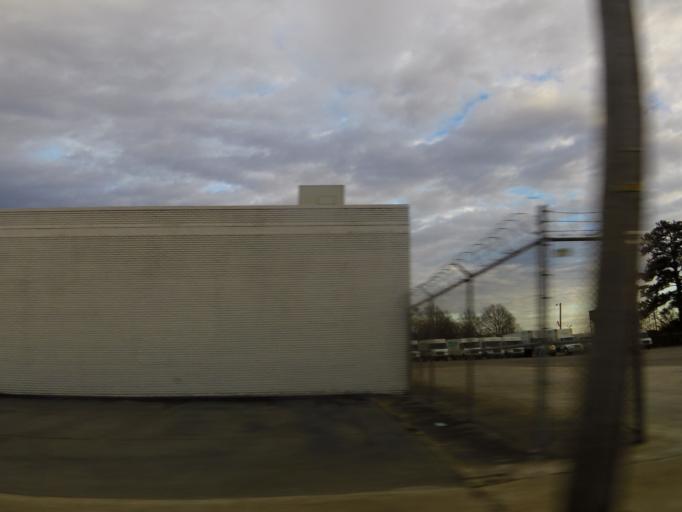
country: US
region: North Carolina
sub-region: Nash County
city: Rocky Mount
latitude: 35.9320
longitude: -77.8014
